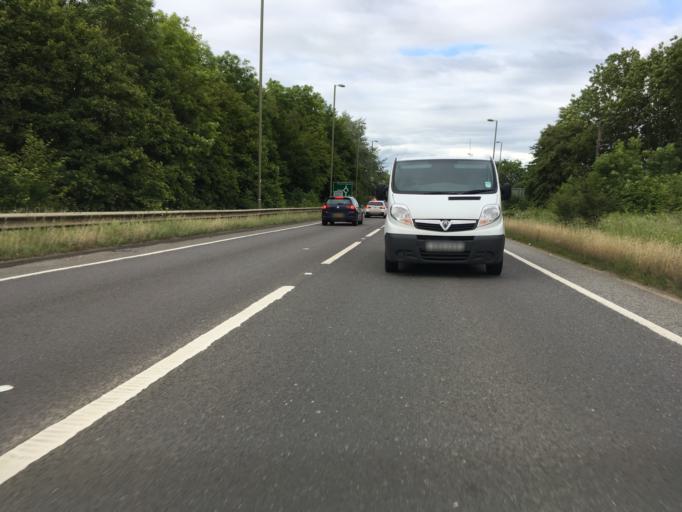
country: GB
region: England
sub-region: Oxfordshire
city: Faringdon
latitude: 51.6484
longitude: -1.5765
